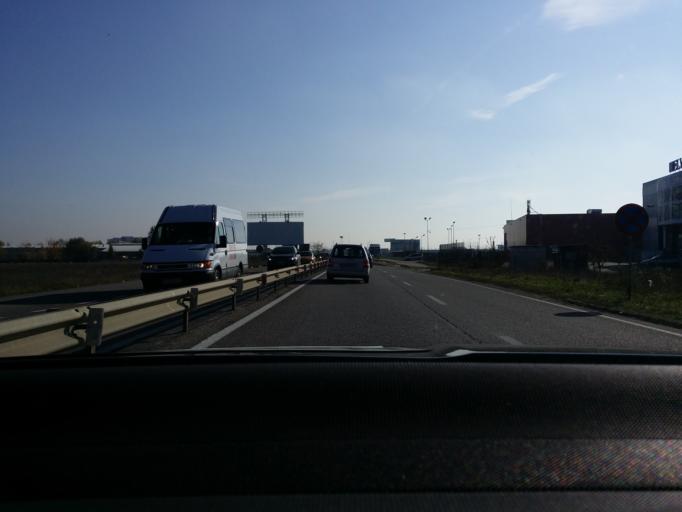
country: RO
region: Prahova
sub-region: Comuna Paulesti
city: Paulesti
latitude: 44.9673
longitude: 25.9646
